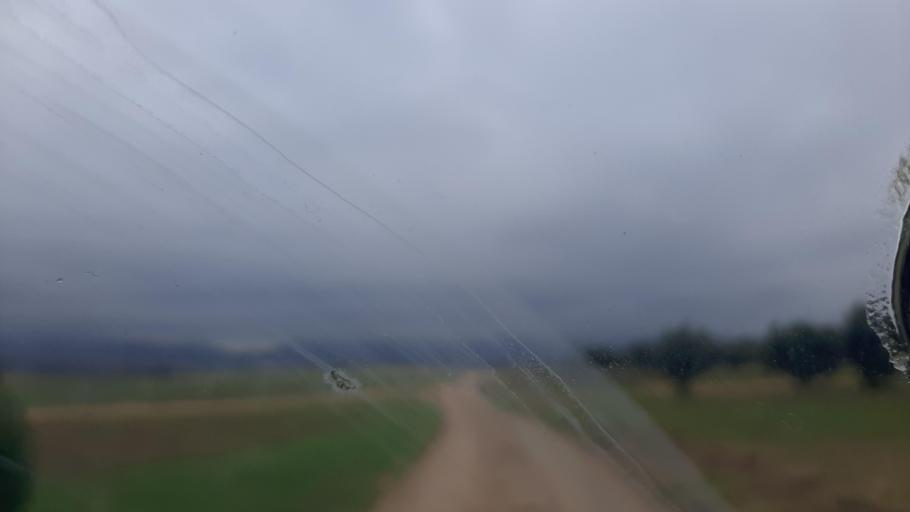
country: TN
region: Tunis
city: La Sebala du Mornag
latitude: 36.5696
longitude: 10.2944
